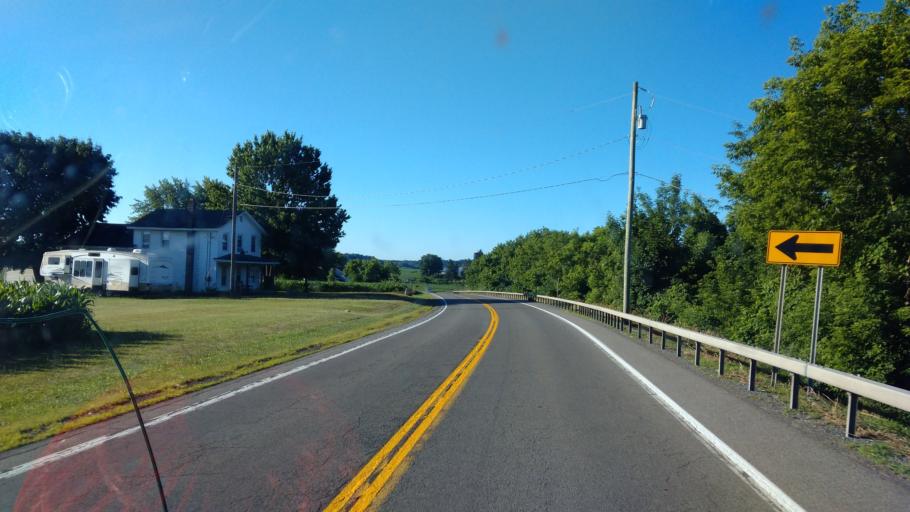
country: US
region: New York
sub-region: Wayne County
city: Lyons
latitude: 43.0388
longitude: -76.9929
